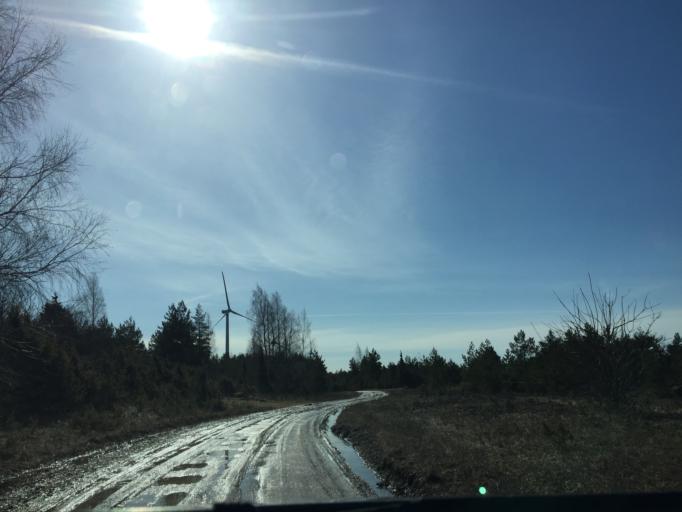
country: EE
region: Laeaene
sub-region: Haapsalu linn
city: Haapsalu
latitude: 58.6453
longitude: 23.5142
